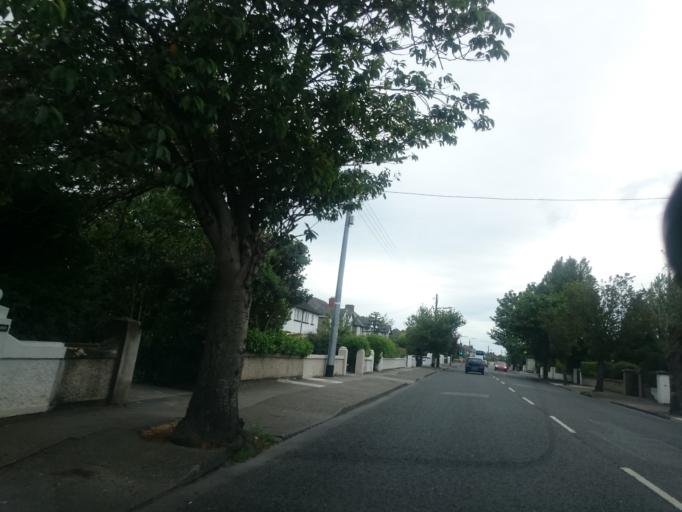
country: IE
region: Leinster
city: Templeogue
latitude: 53.3134
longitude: -6.3078
